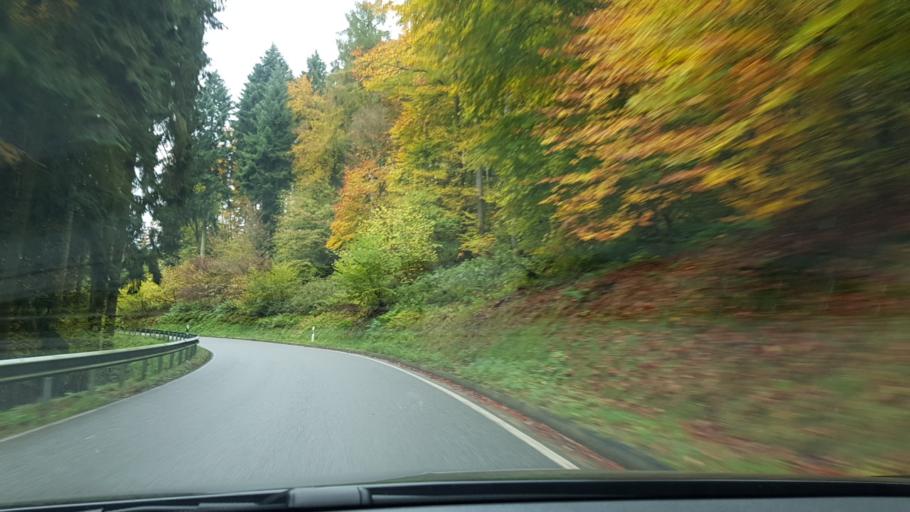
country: DE
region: Rheinland-Pfalz
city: Mehring
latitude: 49.7848
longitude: 6.8355
